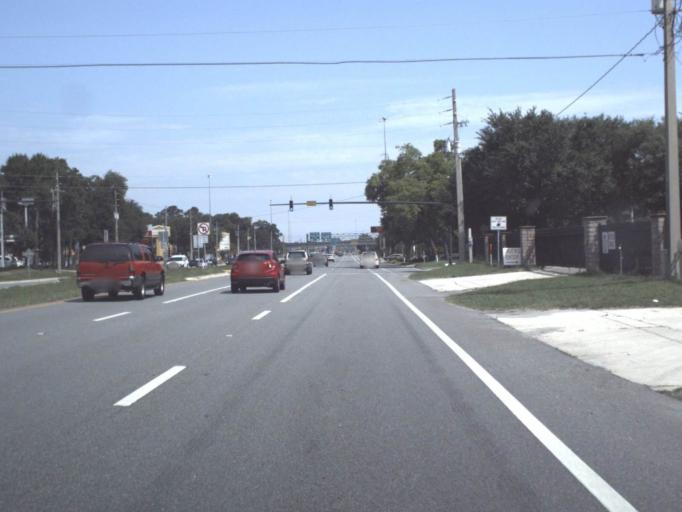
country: US
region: Florida
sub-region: Saint Johns County
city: Fruit Cove
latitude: 30.1716
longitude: -81.5451
